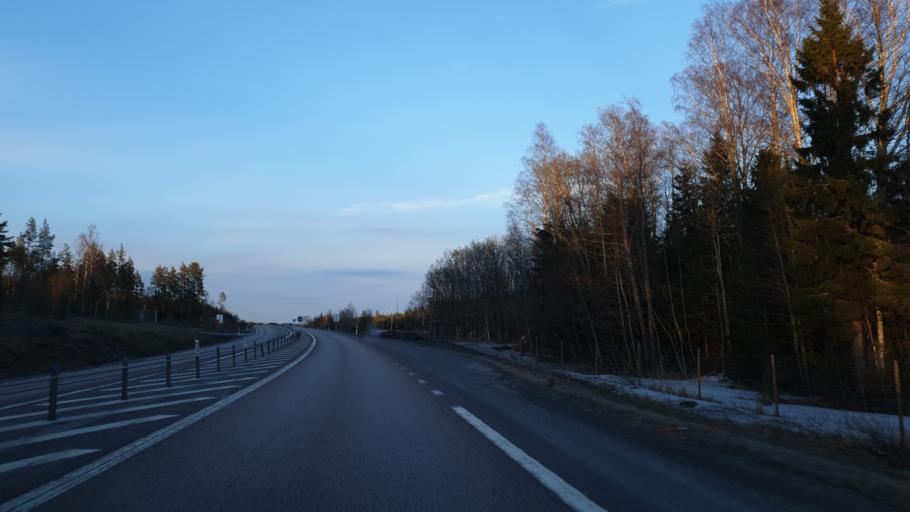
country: SE
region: Vaesternorrland
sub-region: Timra Kommun
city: Soraker
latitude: 62.5473
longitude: 17.6027
